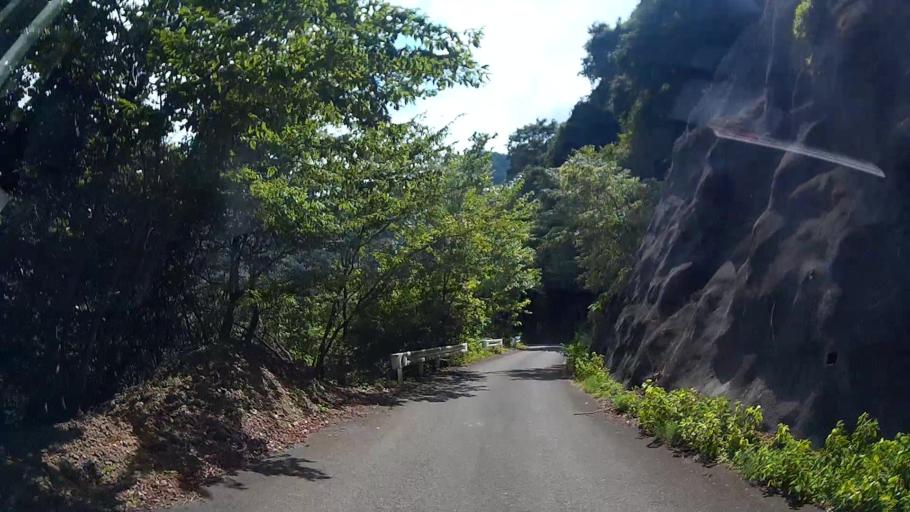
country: JP
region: Saitama
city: Chichibu
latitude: 35.8917
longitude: 139.1032
